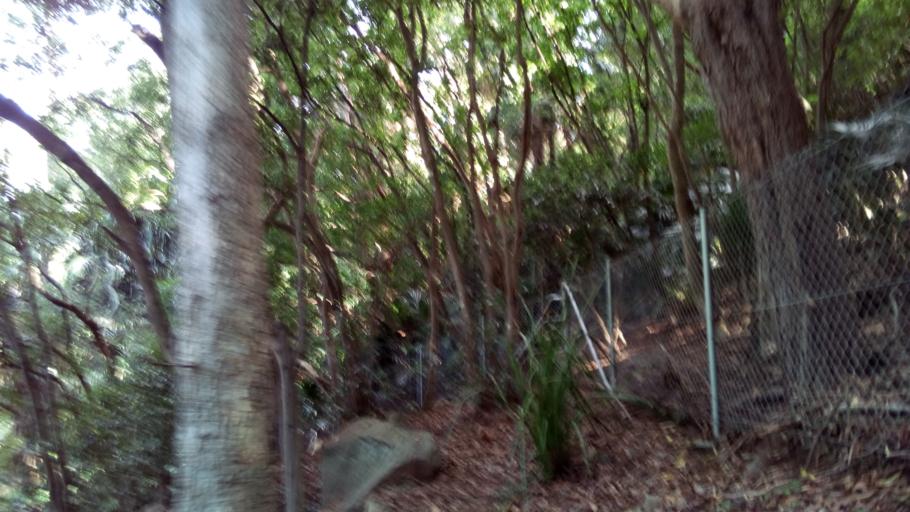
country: AU
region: New South Wales
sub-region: Wollongong
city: Mount Ousley
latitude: -34.3975
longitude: 150.8596
